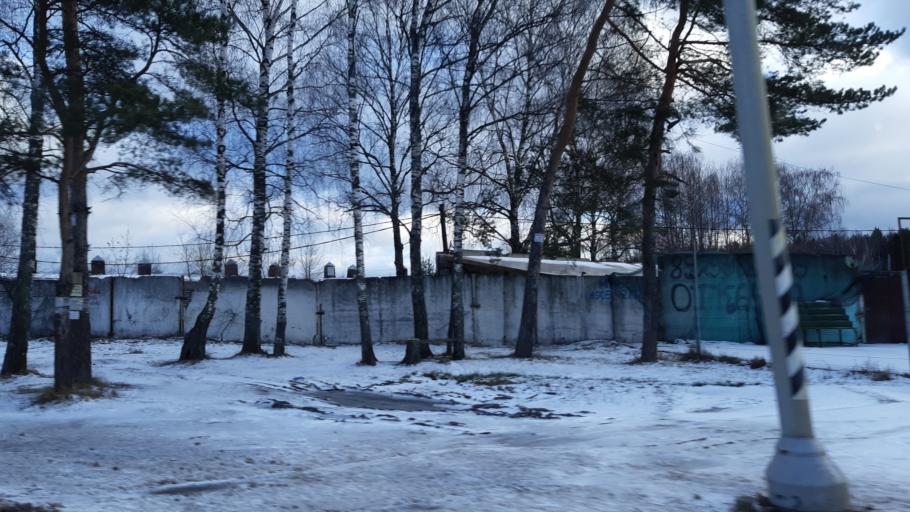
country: RU
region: Moskovskaya
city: Noginsk-9
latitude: 55.9465
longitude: 38.5517
